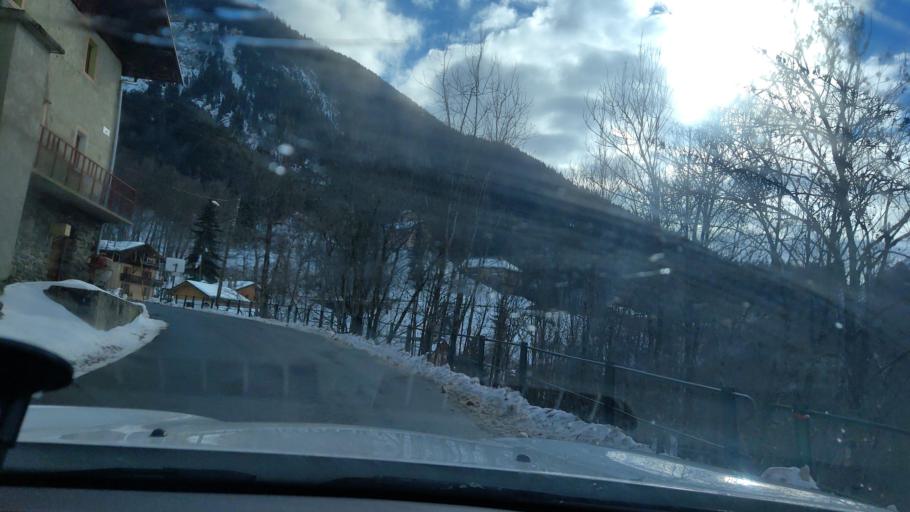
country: FR
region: Rhone-Alpes
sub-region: Departement de la Savoie
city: Saint-Martin-de-Belleville
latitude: 45.4280
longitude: 6.4988
